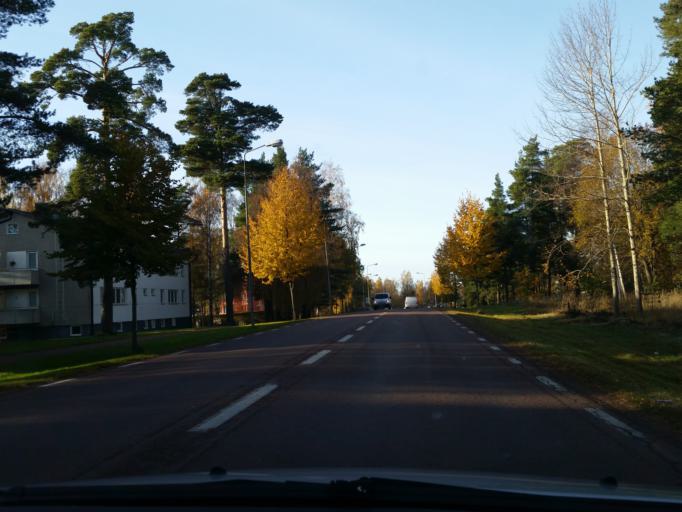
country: AX
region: Mariehamns stad
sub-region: Mariehamn
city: Mariehamn
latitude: 60.1054
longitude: 19.9353
